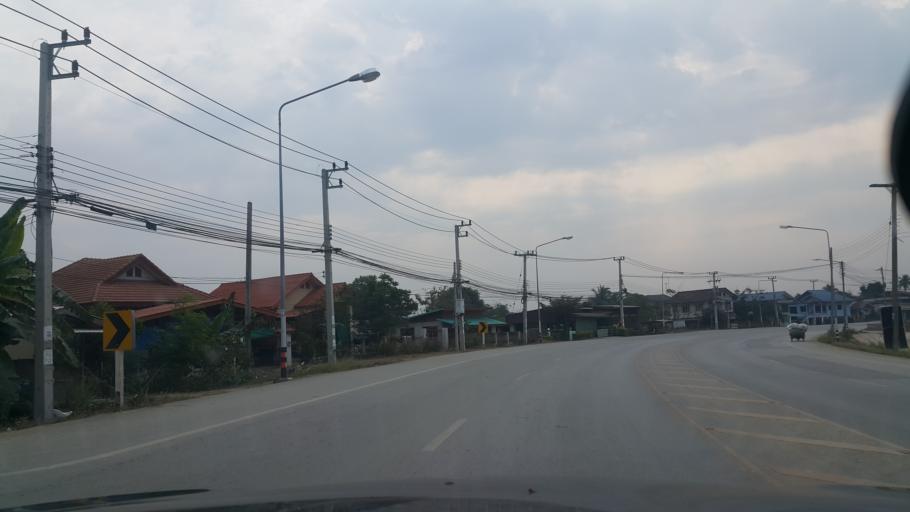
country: TH
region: Sukhothai
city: Si Samrong
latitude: 17.1600
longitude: 99.8706
